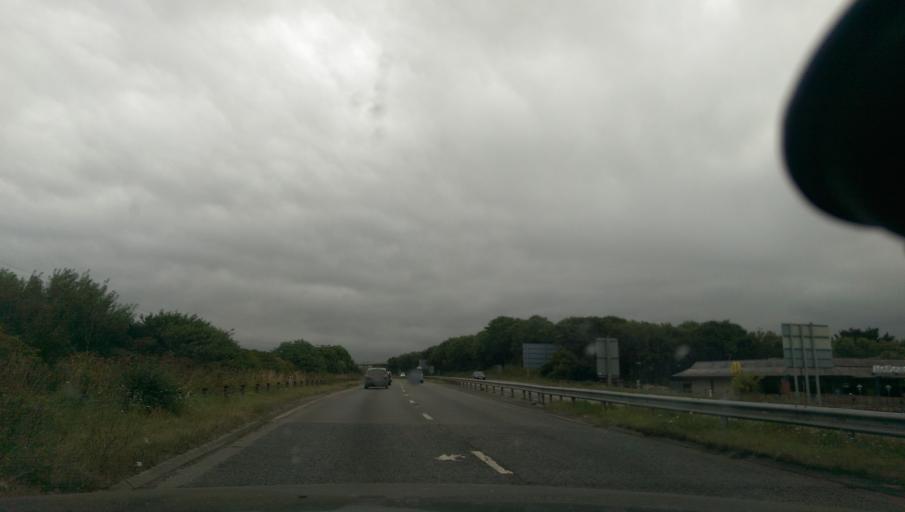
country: GB
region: England
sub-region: Cornwall
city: Penzance
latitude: 50.1300
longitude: -5.5115
